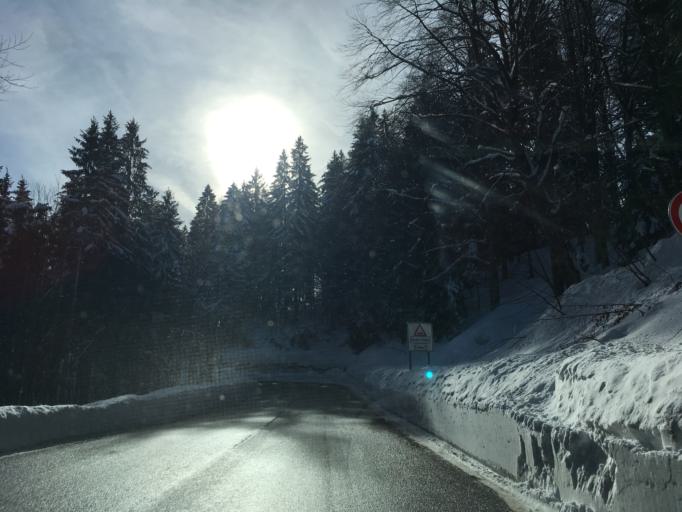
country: DE
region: Bavaria
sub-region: Upper Bavaria
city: Bayrischzell
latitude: 47.6804
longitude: 12.0342
